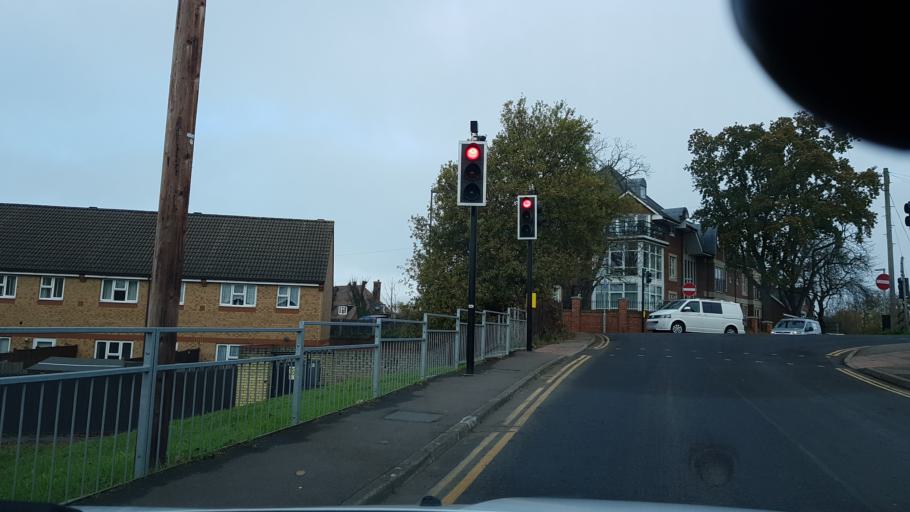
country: GB
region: England
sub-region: Central Bedfordshire
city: Biggleswade
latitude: 52.0890
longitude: -0.2626
